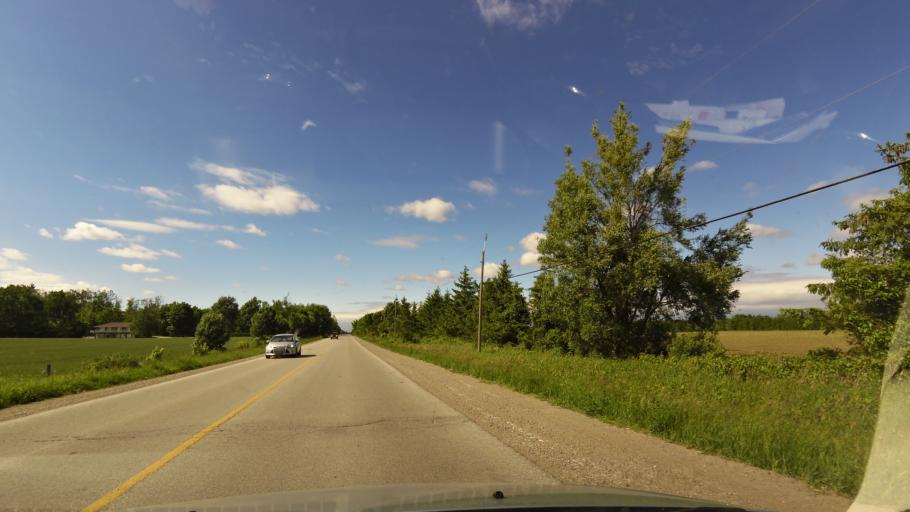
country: CA
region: Ontario
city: Bradford West Gwillimbury
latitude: 44.1444
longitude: -79.6114
